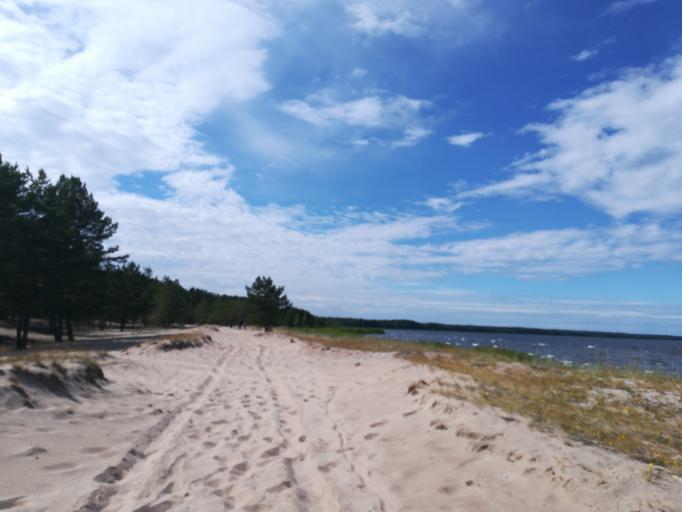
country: RU
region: Leningrad
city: Ust'-Luga
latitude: 59.6803
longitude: 28.2346
